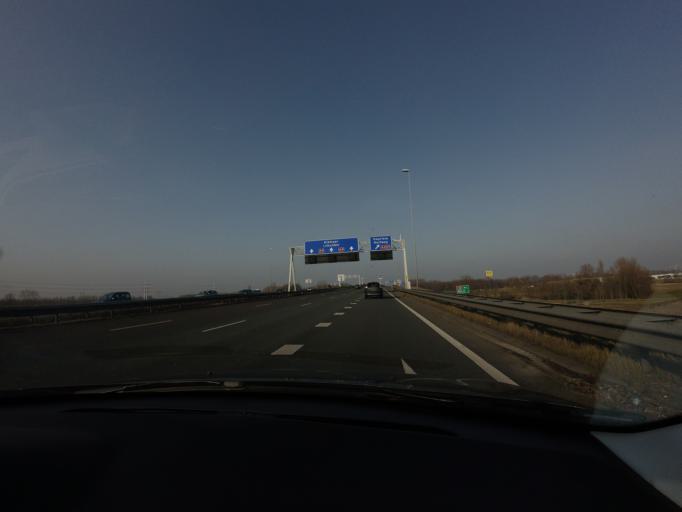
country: NL
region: North Holland
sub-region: Gemeente Haarlem
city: Haarlem
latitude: 52.3791
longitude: 4.7085
